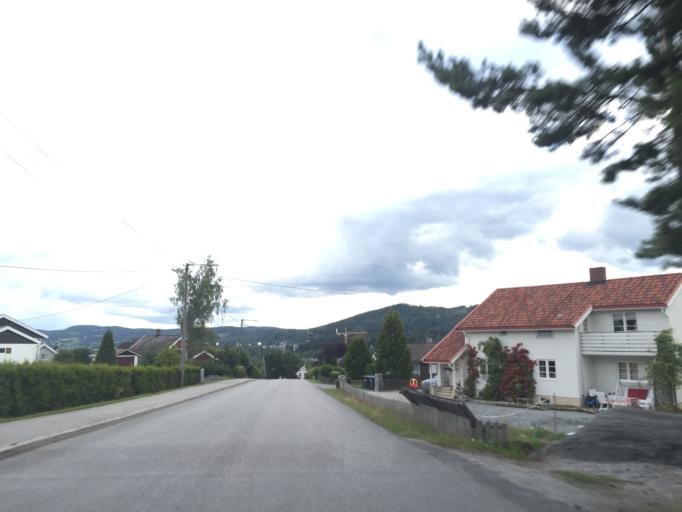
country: NO
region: Hedmark
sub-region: Kongsvinger
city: Kongsvinger
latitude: 60.1863
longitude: 11.9968
